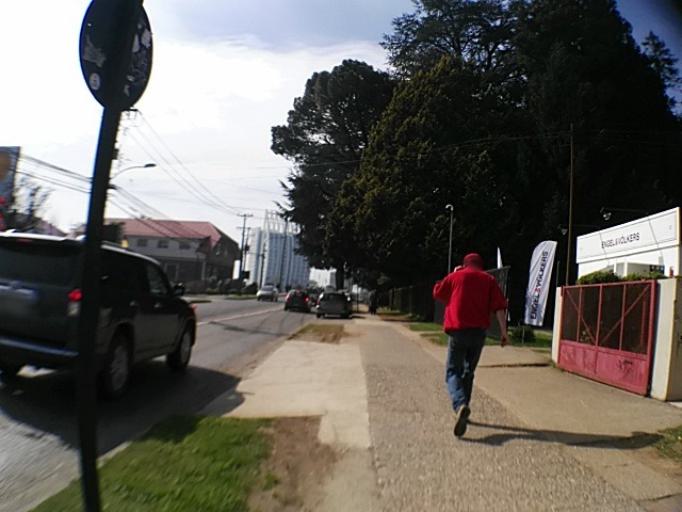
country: CL
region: Los Rios
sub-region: Provincia de Valdivia
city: Valdivia
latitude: -39.8111
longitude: -73.2514
